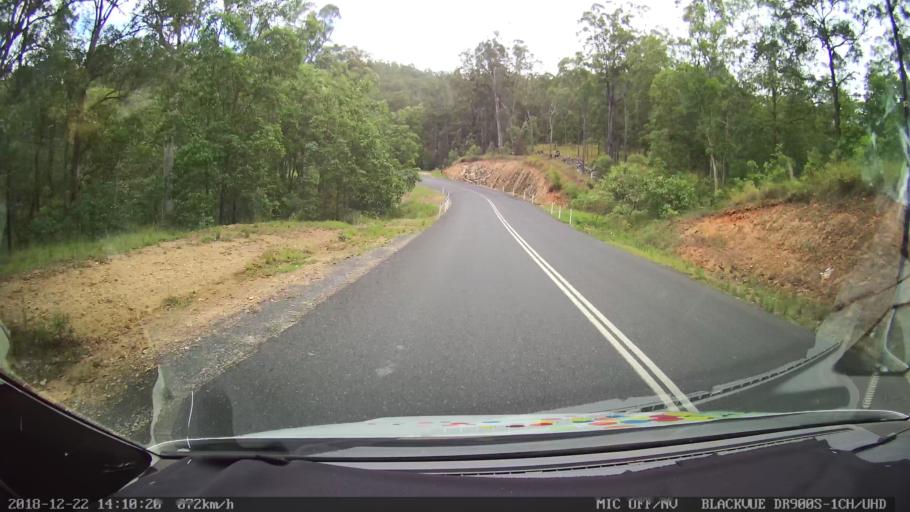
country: AU
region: New South Wales
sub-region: Clarence Valley
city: Coutts Crossing
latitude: -29.9921
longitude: 152.7098
